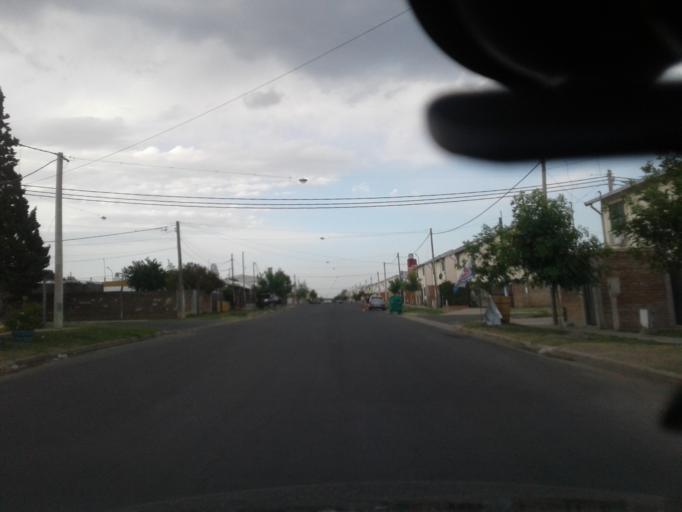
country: AR
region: Santa Fe
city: Granadero Baigorria
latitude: -32.8846
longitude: -60.7242
